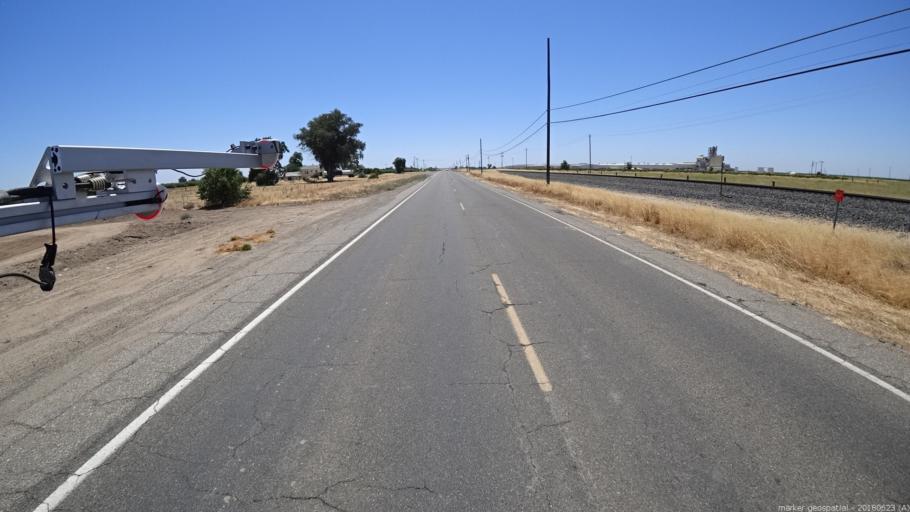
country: US
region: California
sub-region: Madera County
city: Chowchilla
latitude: 37.1009
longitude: -120.2275
